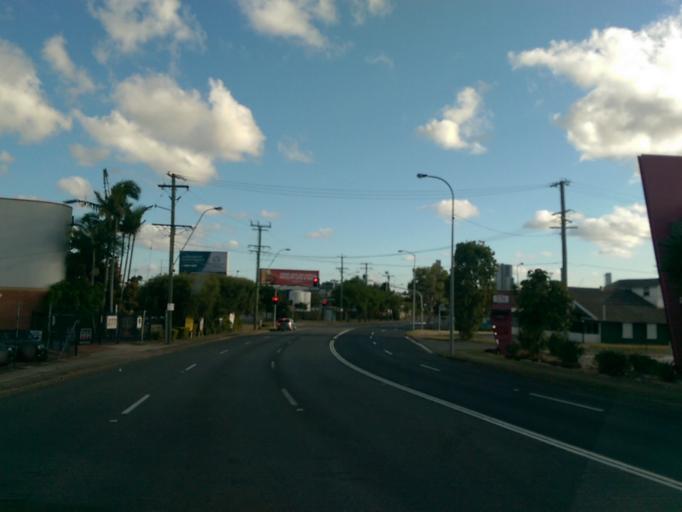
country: AU
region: Queensland
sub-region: Brisbane
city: Wooloowin
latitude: -27.4339
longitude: 153.0425
